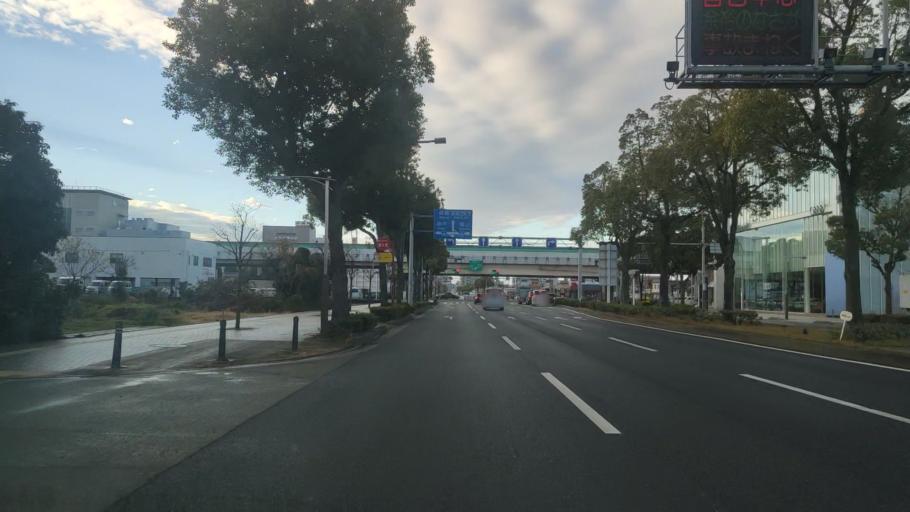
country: JP
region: Hyogo
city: Himeji
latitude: 34.8129
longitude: 134.6831
